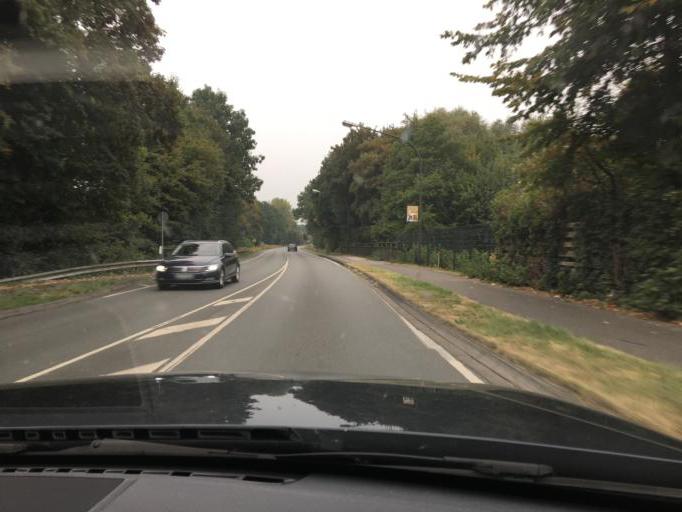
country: DE
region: North Rhine-Westphalia
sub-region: Regierungsbezirk Munster
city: Ladbergen
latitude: 52.1343
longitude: 7.7327
